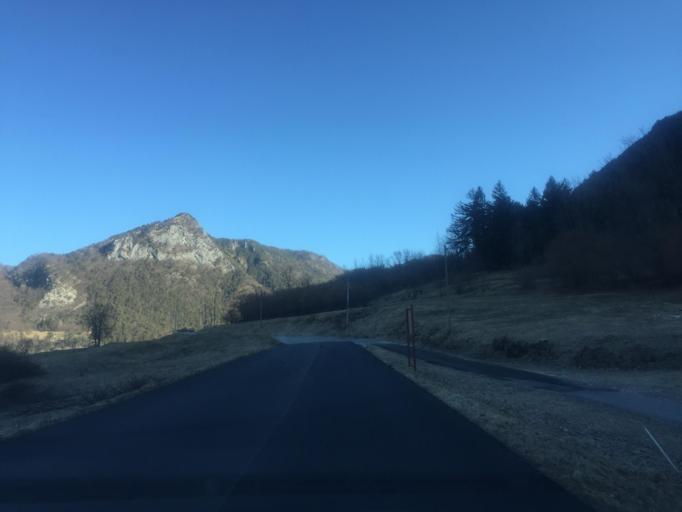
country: IT
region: Friuli Venezia Giulia
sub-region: Provincia di Udine
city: Tolmezzo
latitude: 46.4219
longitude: 13.0512
